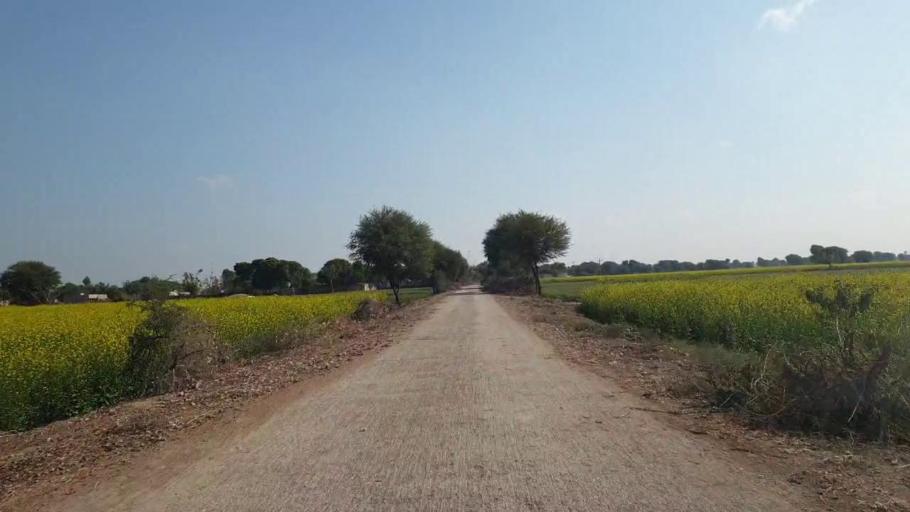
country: PK
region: Sindh
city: Shahpur Chakar
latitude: 26.0564
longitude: 68.5958
